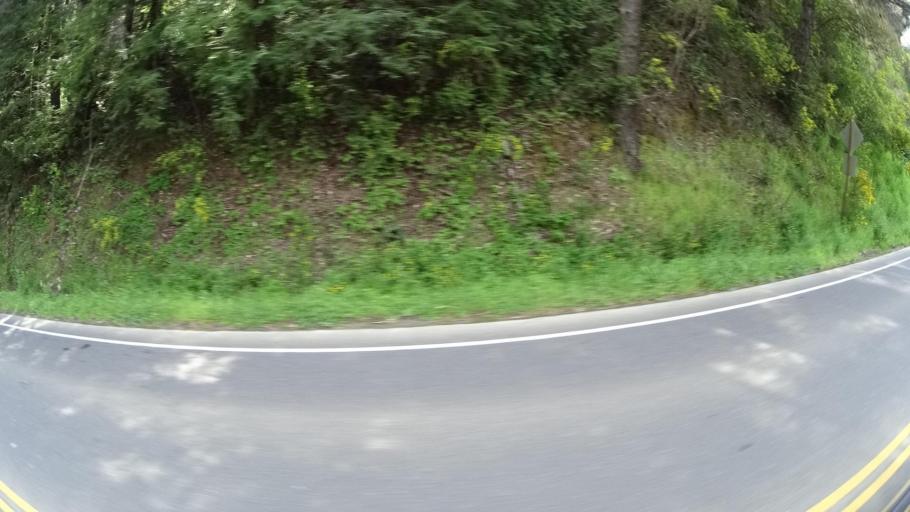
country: US
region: California
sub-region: Humboldt County
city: Redway
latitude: 40.1283
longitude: -123.8204
